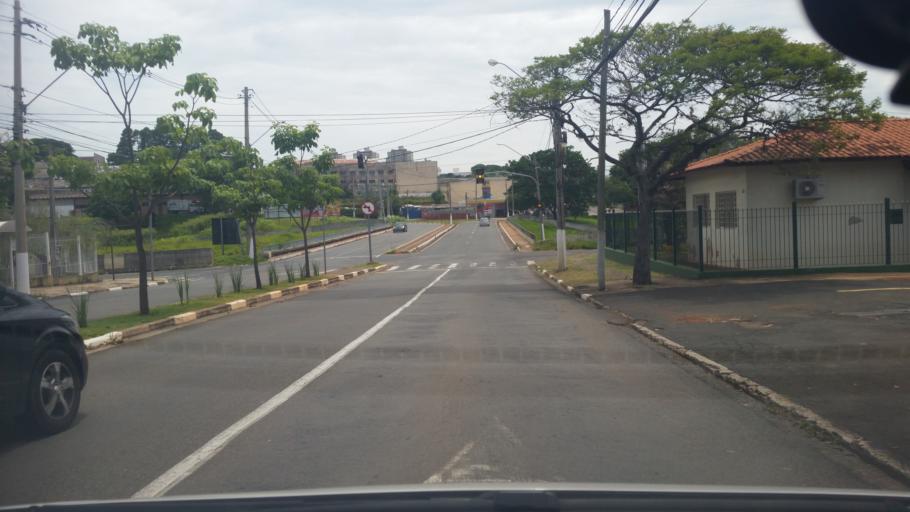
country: BR
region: Sao Paulo
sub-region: Campinas
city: Campinas
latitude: -22.8414
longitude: -47.0531
